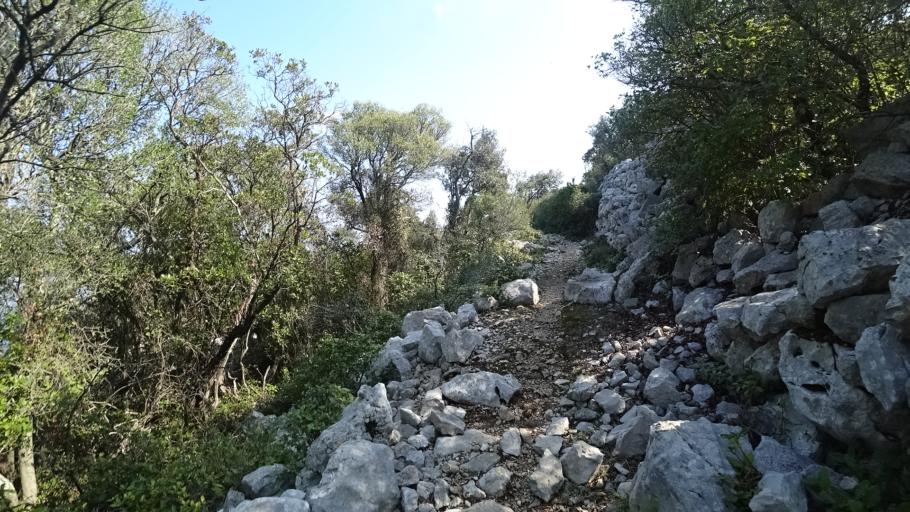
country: HR
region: Primorsko-Goranska
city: Mali Losinj
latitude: 44.4952
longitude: 14.5287
